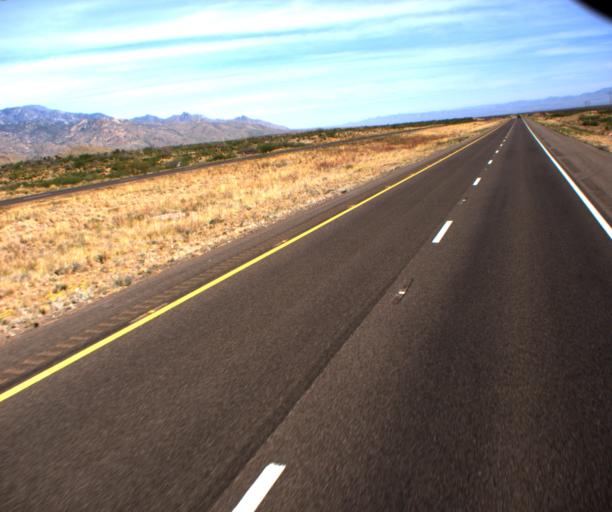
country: US
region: Arizona
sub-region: Graham County
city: Swift Trail Junction
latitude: 32.5702
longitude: -109.6806
